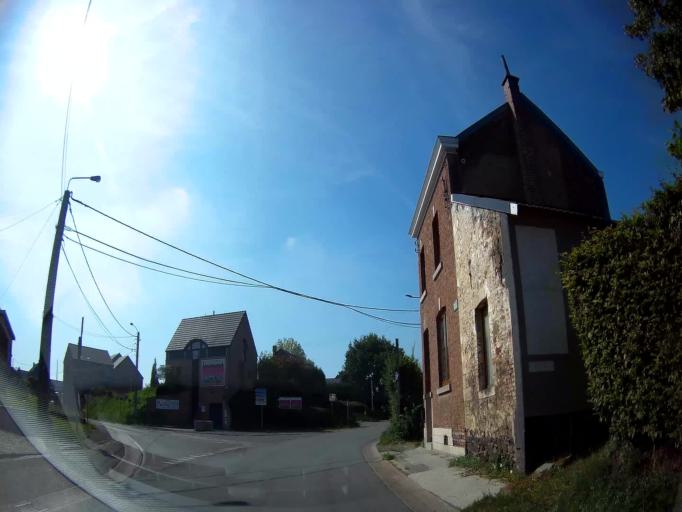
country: BE
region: Wallonia
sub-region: Province de Liege
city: Verlaine
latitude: 50.5918
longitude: 5.3410
